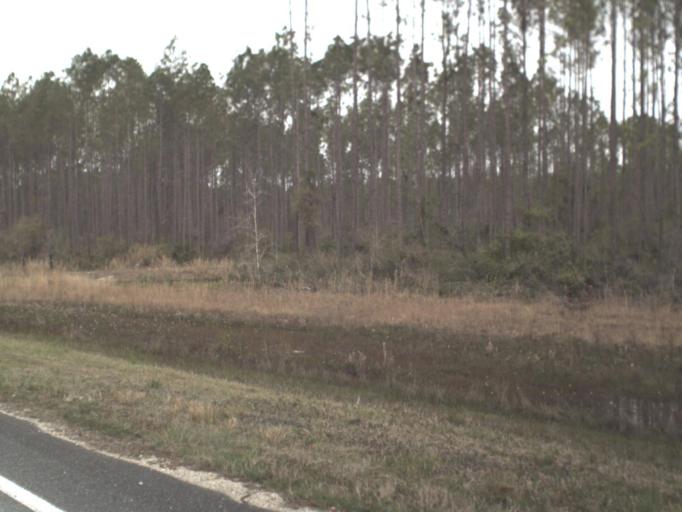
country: US
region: Florida
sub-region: Leon County
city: Woodville
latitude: 30.1961
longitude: -84.1474
